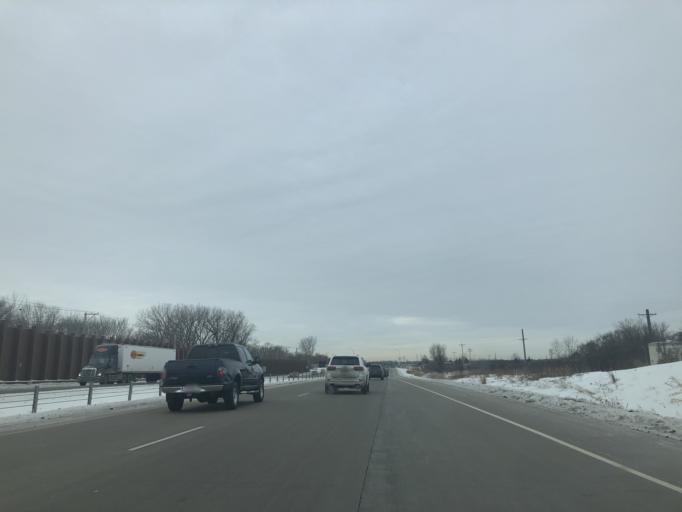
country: US
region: Minnesota
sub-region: Ramsey County
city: New Brighton
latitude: 45.0820
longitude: -93.1792
